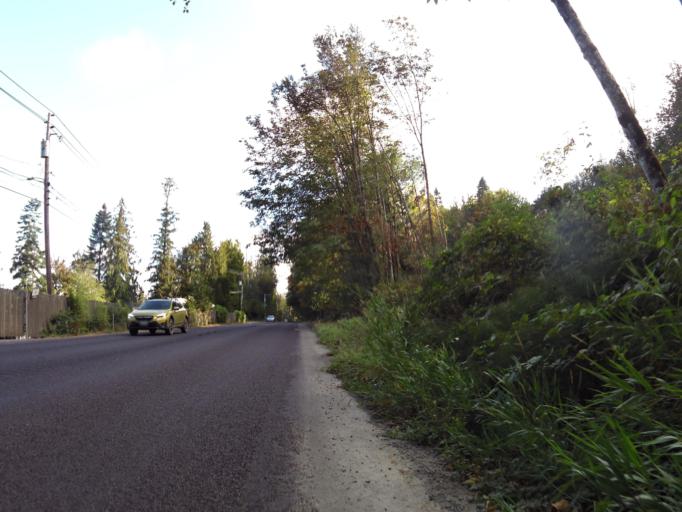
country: US
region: Washington
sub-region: Mason County
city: Belfair
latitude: 47.4246
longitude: -122.8583
